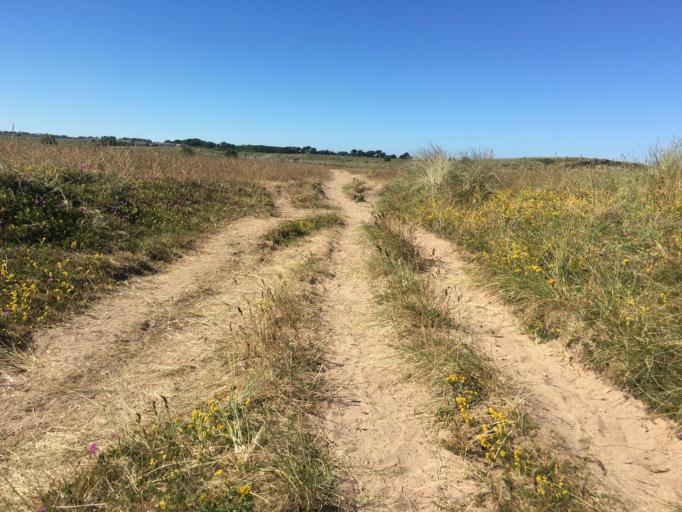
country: GB
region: England
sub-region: Northumberland
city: Beadnell
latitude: 55.5362
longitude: -1.6405
